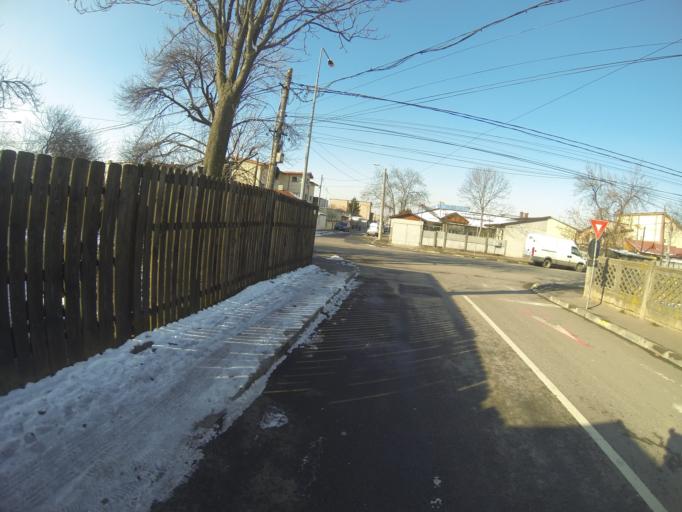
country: RO
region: Bucuresti
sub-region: Municipiul Bucuresti
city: Bucuresti
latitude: 44.3968
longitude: 26.0618
